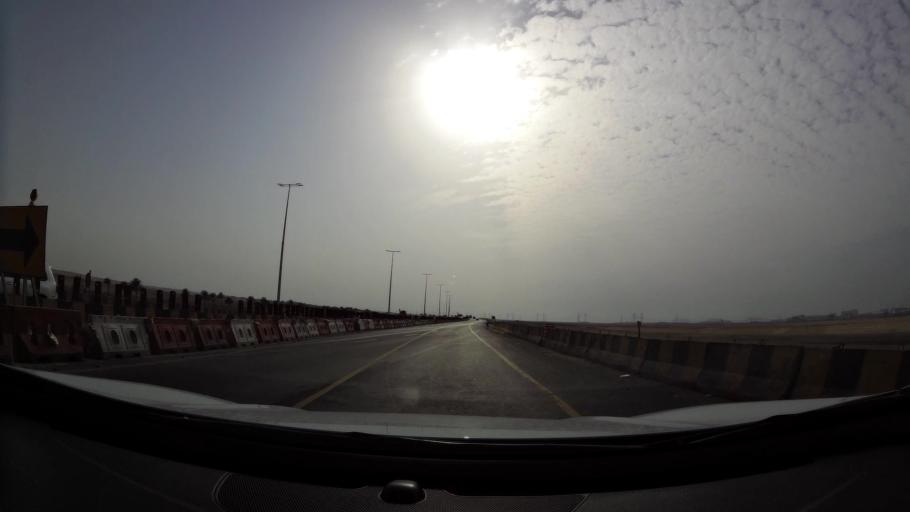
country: AE
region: Abu Dhabi
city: Abu Dhabi
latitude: 24.2711
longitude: 54.5028
